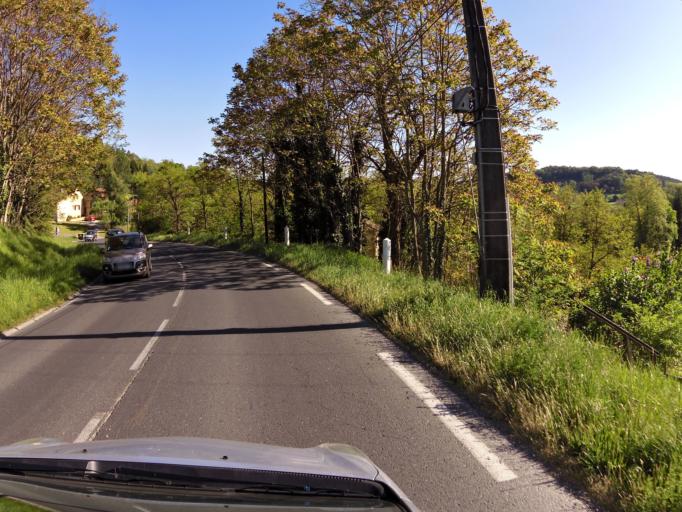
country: FR
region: Aquitaine
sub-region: Departement de la Dordogne
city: Sarlat-la-Caneda
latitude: 44.9137
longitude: 1.2061
